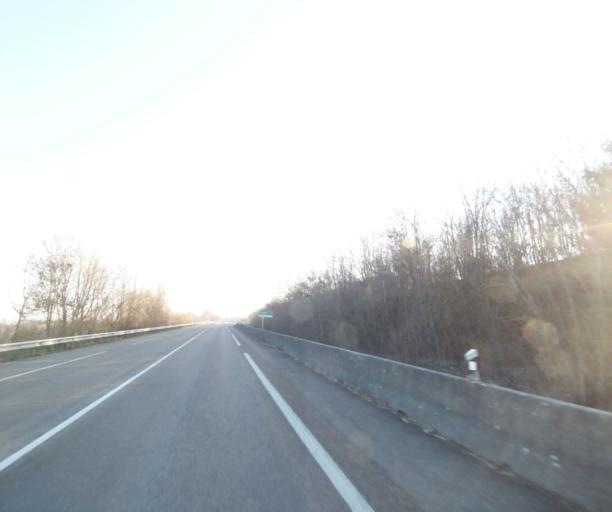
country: FR
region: Champagne-Ardenne
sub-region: Departement de la Haute-Marne
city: Chevillon
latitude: 48.5365
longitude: 5.0890
